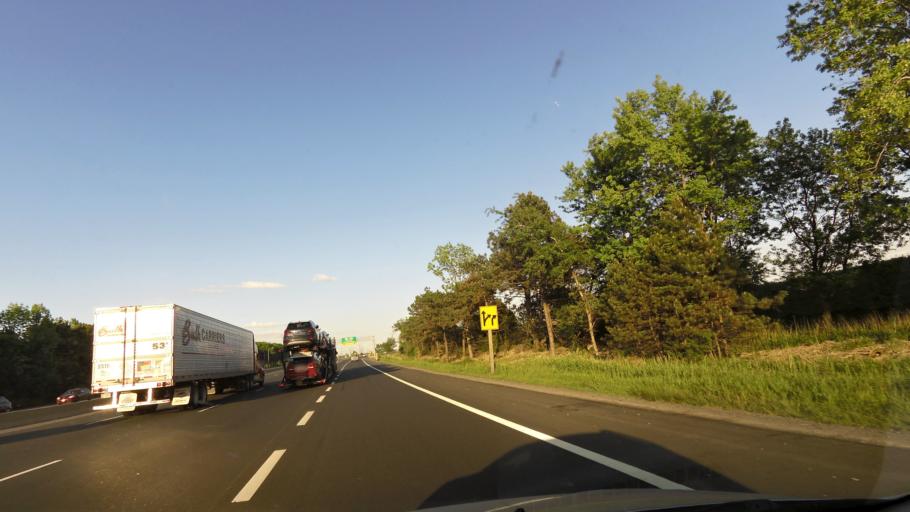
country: CA
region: Ontario
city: Oshawa
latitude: 43.9019
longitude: -78.6361
